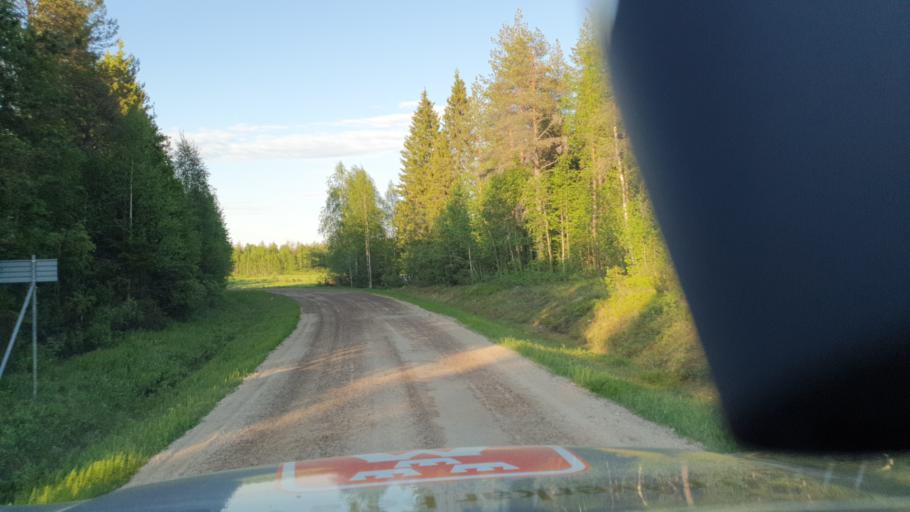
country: FI
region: Lapland
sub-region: Torniolaakso
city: Ylitornio
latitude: 66.1537
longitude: 23.6802
